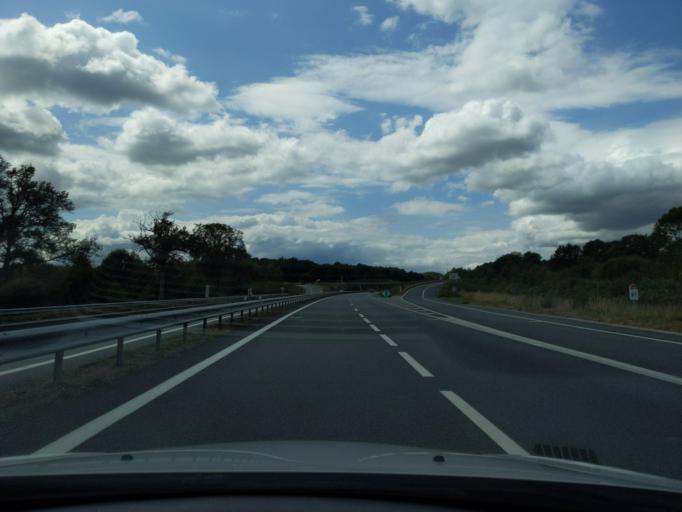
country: FR
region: Limousin
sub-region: Departement de la Creuse
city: Ajain
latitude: 46.2037
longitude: 2.0771
